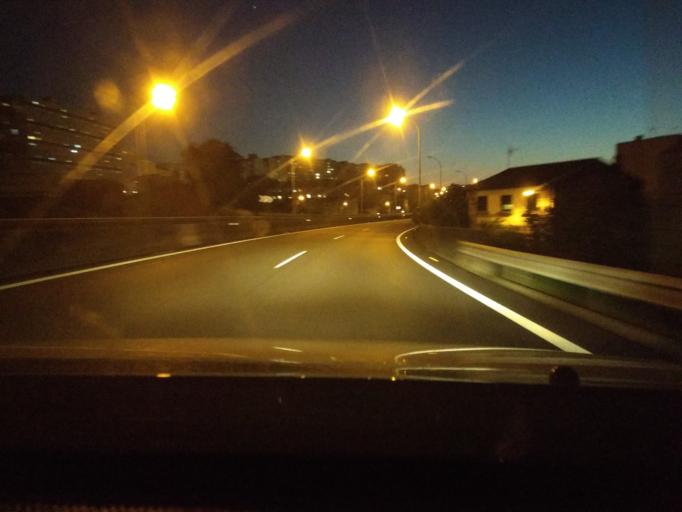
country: ES
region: Galicia
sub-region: Provincia de Pontevedra
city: Vigo
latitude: 42.2467
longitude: -8.6963
